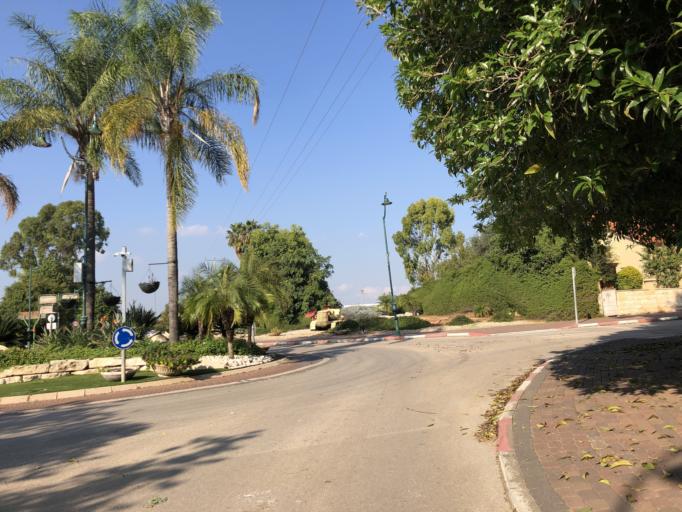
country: IL
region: Central District
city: Jaljulya
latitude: 32.1355
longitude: 34.9242
